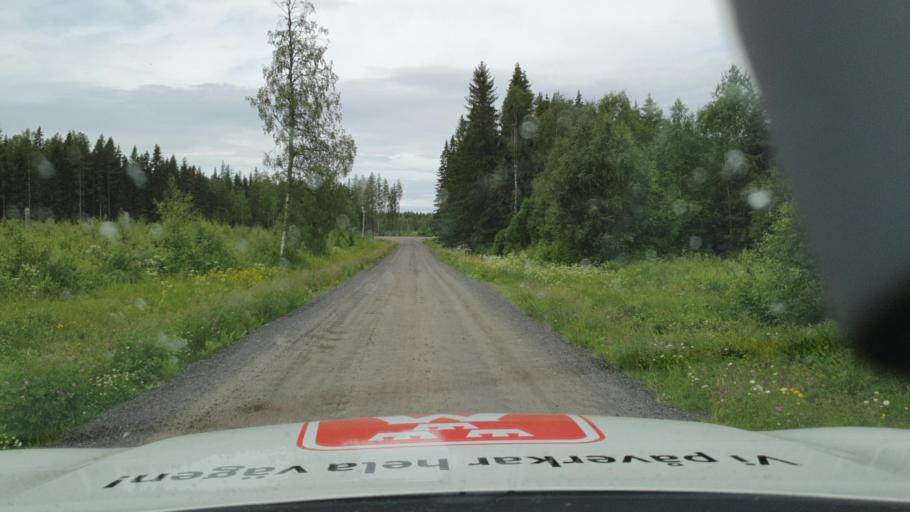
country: SE
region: Vaesterbotten
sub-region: Skelleftea Kommun
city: Burtraesk
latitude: 64.4021
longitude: 20.5515
